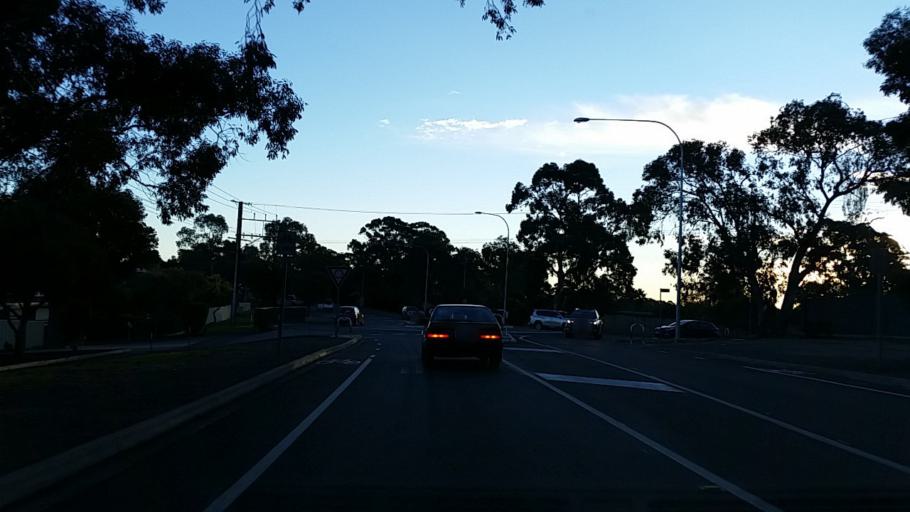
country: AU
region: South Australia
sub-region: Onkaparinga
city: Bedford Park
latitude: -35.0487
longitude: 138.5846
